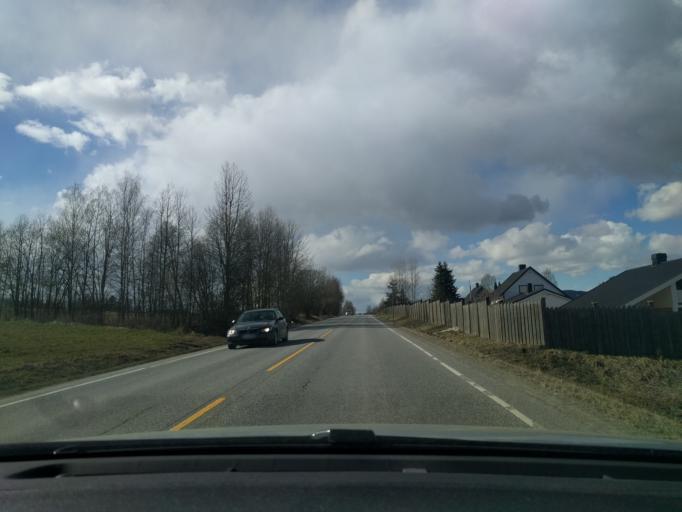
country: NO
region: Hedmark
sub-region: Hamar
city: Hamar
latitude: 60.8327
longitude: 11.0636
